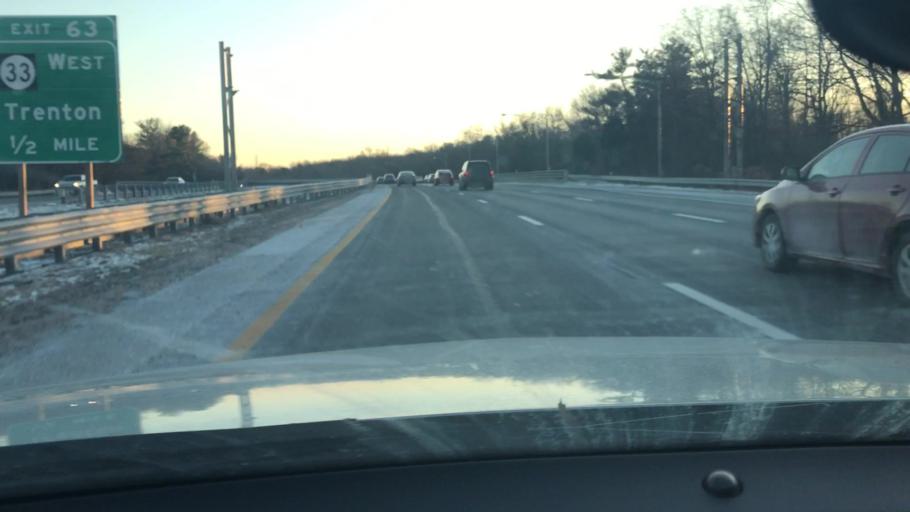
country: US
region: New Jersey
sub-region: Mercer County
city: Mercerville
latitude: 40.2436
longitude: -74.7010
